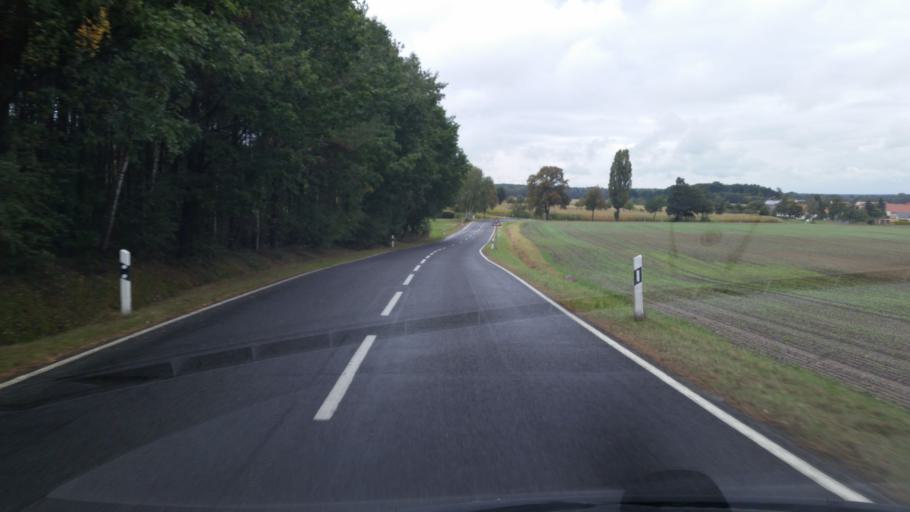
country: DE
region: Saxony
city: Neukirch
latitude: 51.3102
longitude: 14.0346
